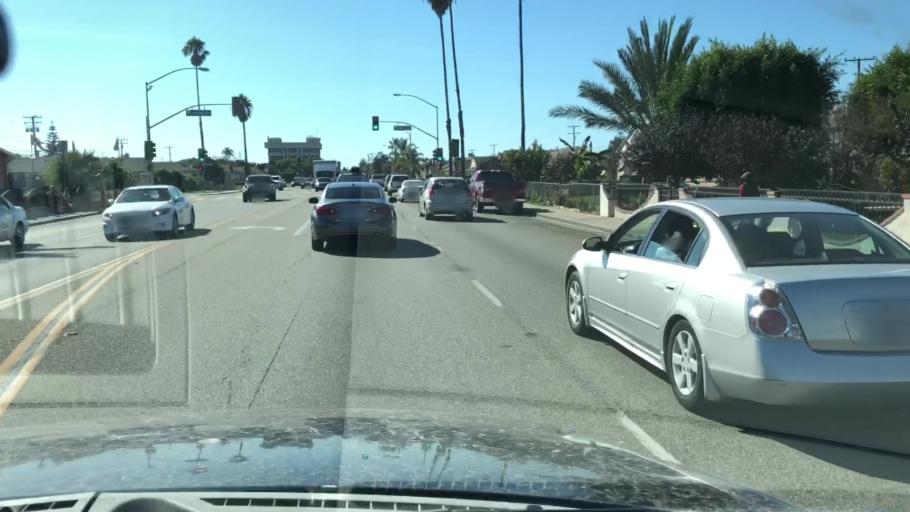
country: US
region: California
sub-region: Ventura County
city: Oxnard
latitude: 34.1734
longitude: -119.1719
